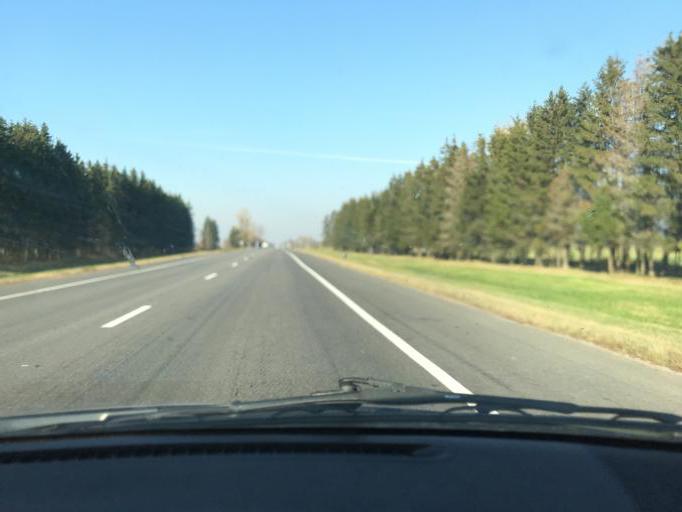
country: BY
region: Mogilev
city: Shklow
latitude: 54.2651
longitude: 30.4501
